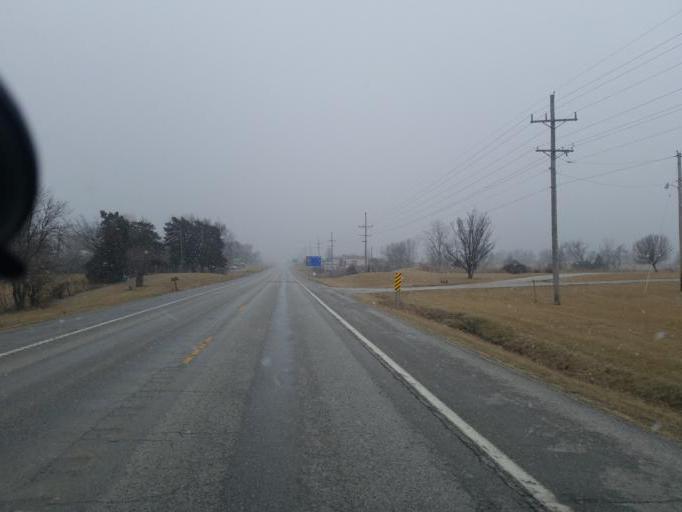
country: US
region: Missouri
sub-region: Adair County
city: Kirksville
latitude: 40.2550
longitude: -92.5826
